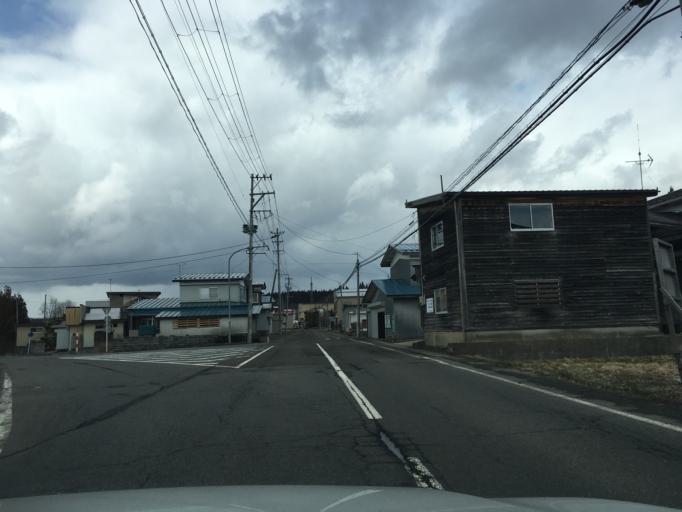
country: JP
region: Akita
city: Takanosu
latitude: 40.1577
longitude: 140.3334
